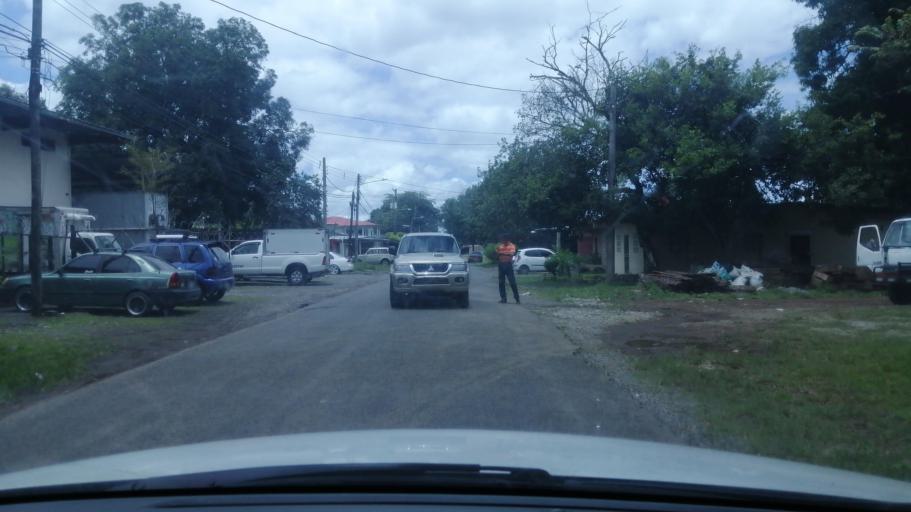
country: PA
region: Chiriqui
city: David
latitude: 8.4409
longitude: -82.4286
